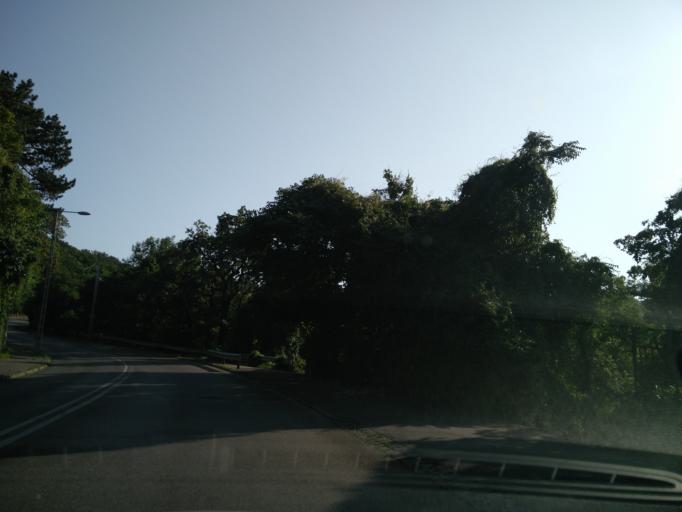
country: HU
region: Budapest
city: Budapest XII. keruelet
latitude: 47.5049
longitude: 18.9907
